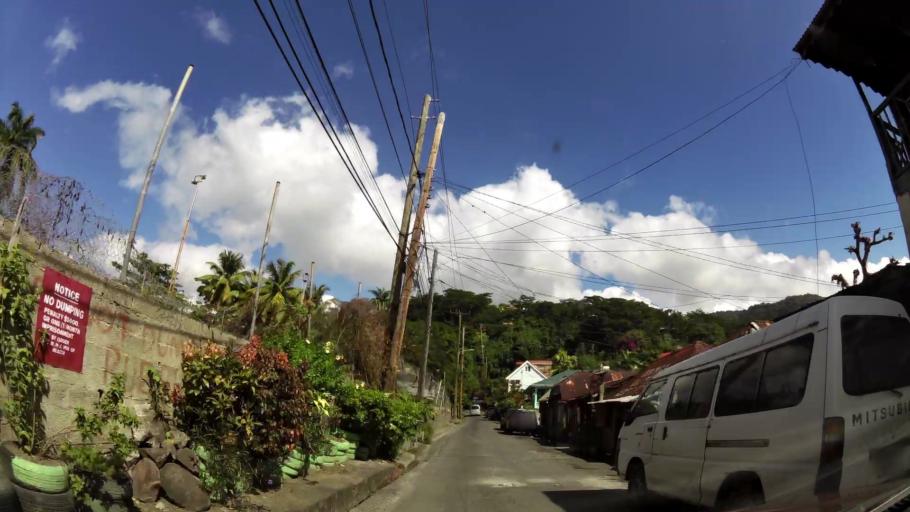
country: DM
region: Saint George
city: Roseau
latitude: 15.2955
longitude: -61.3837
